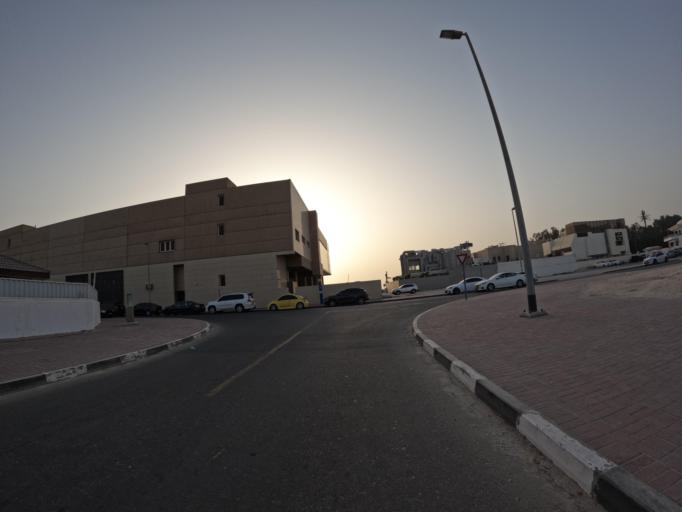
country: AE
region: Dubai
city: Dubai
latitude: 25.1983
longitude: 55.2394
